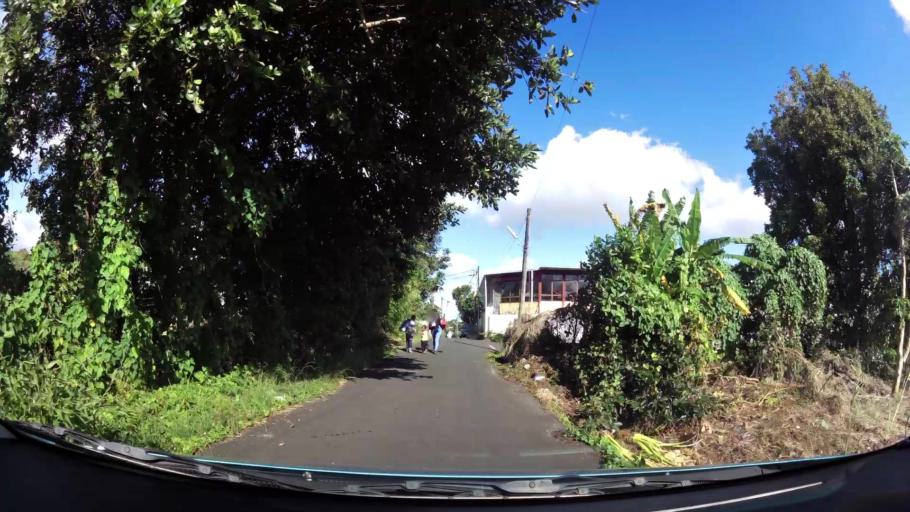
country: MU
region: Plaines Wilhems
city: Curepipe
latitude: -20.2982
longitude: 57.5129
